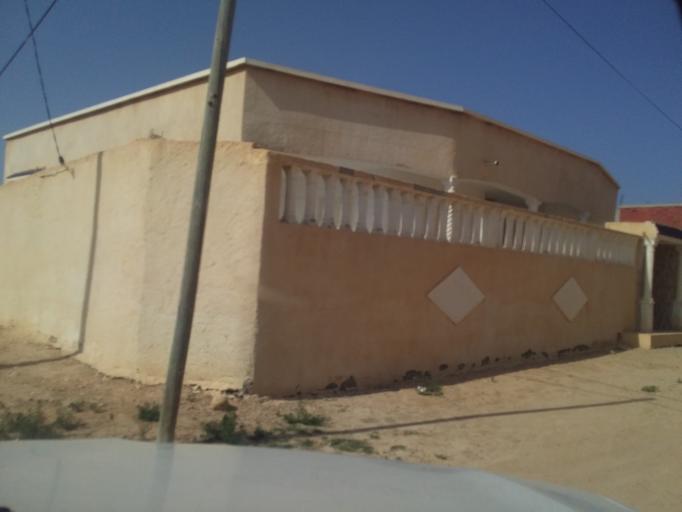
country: TN
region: Qabis
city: Gabes
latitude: 33.6321
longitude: 10.2853
